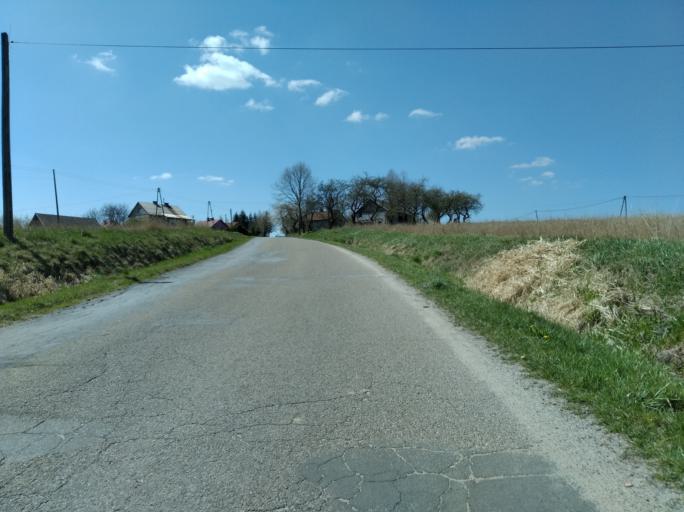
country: PL
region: Subcarpathian Voivodeship
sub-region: Powiat strzyzowski
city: Wisniowa
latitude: 49.9062
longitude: 21.6746
